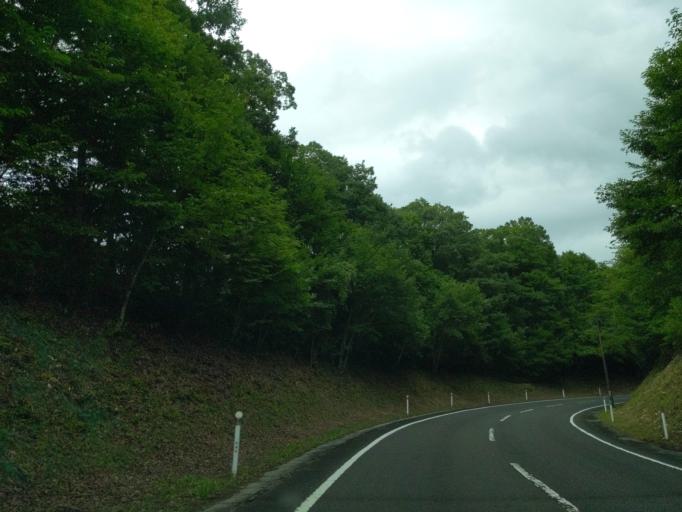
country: JP
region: Tochigi
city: Kuroiso
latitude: 37.2434
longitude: 140.0704
